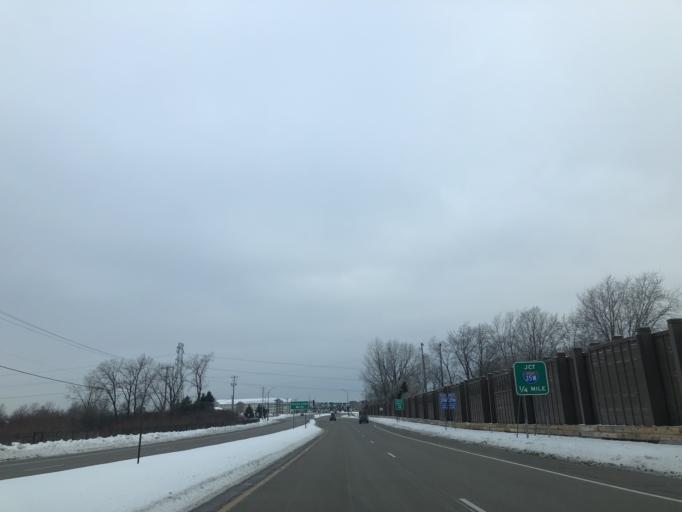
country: US
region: Minnesota
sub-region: Ramsey County
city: New Brighton
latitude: 45.0793
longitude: -93.1790
